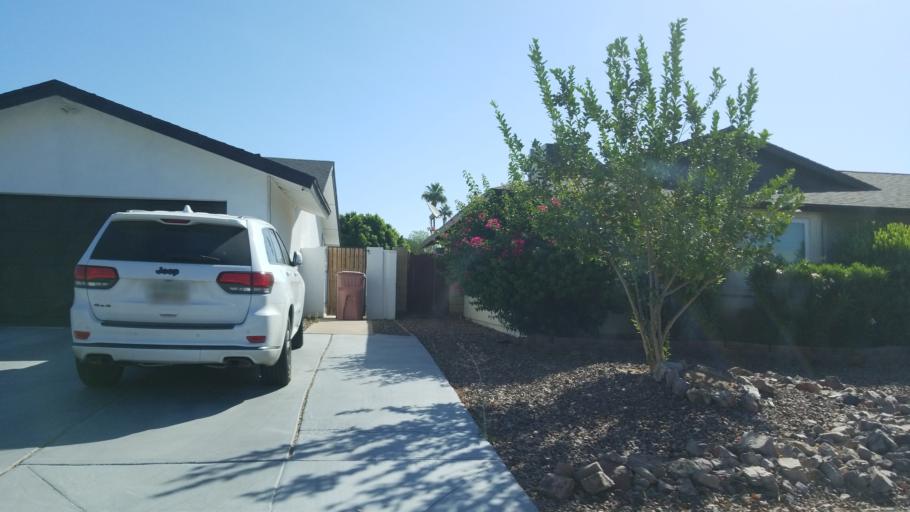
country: US
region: Arizona
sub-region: Maricopa County
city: Scottsdale
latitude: 33.4917
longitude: -111.8943
